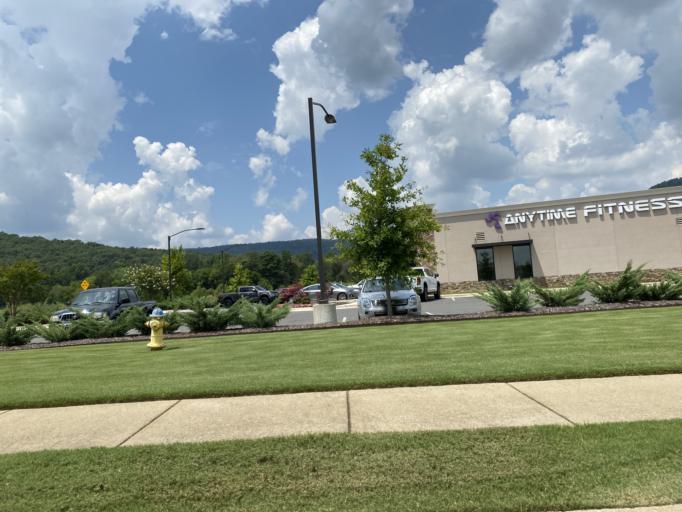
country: US
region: Alabama
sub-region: Madison County
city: Owens Cross Roads
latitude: 34.6576
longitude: -86.4890
